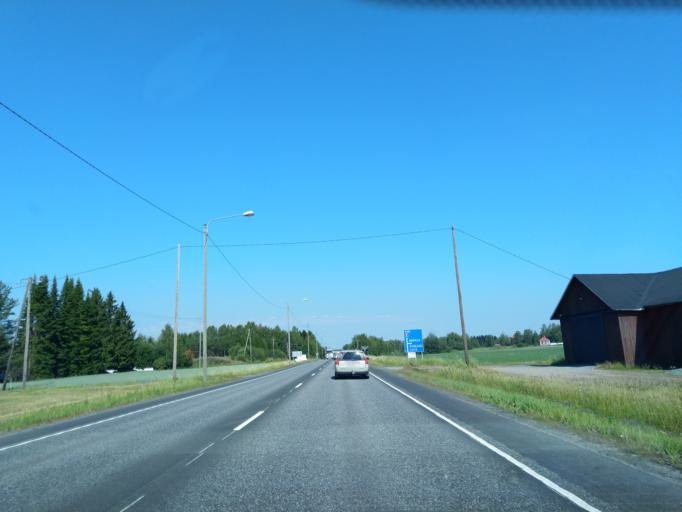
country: FI
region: Satakunta
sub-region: Pori
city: Nakkila
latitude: 61.3569
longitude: 22.0030
